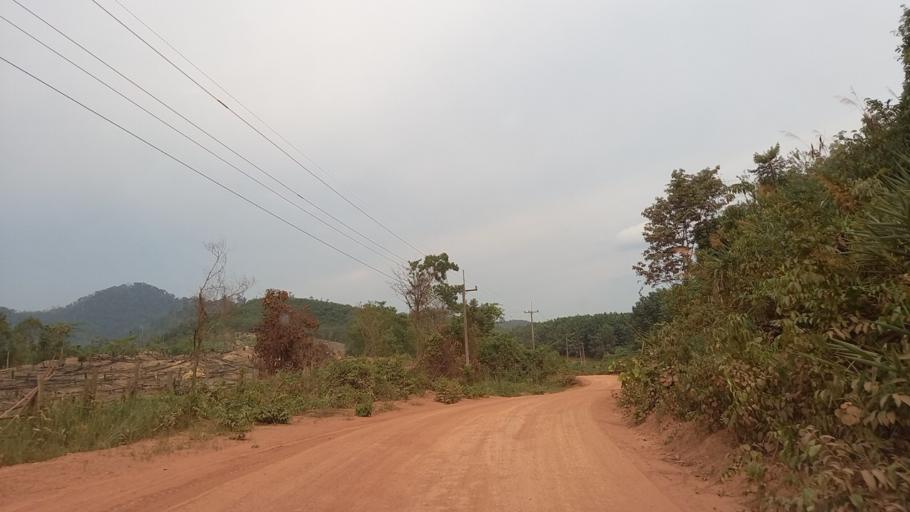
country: LA
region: Bolikhamxai
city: Bolikhan
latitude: 18.5286
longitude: 103.8223
